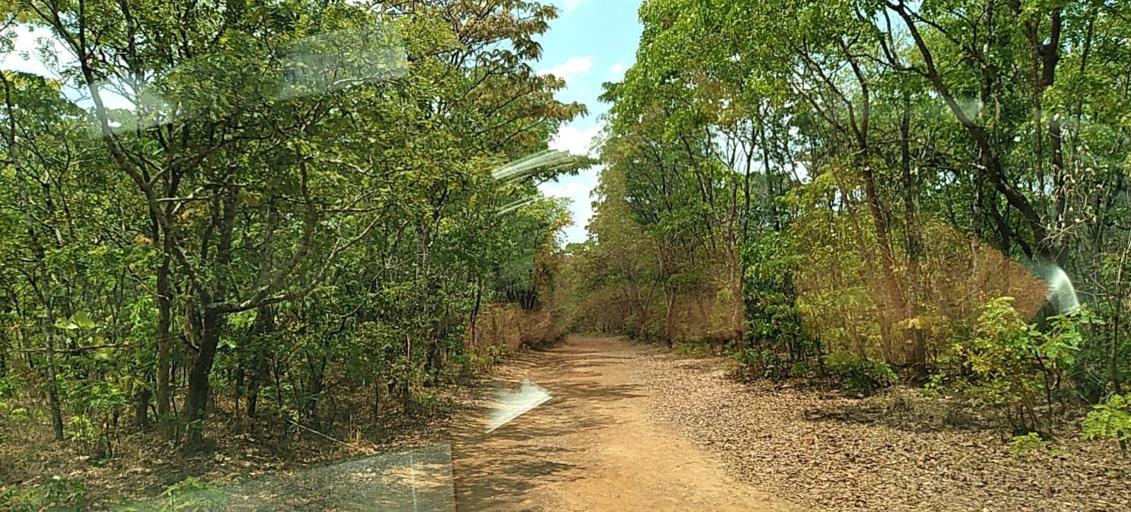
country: ZM
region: Copperbelt
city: Chililabombwe
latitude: -12.4933
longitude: 27.6358
